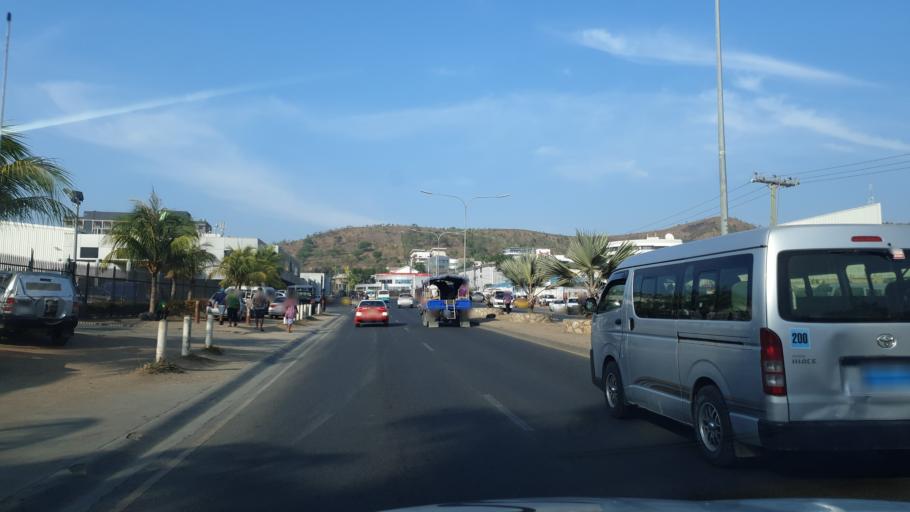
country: PG
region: National Capital
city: Port Moresby
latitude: -9.4436
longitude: 147.1849
